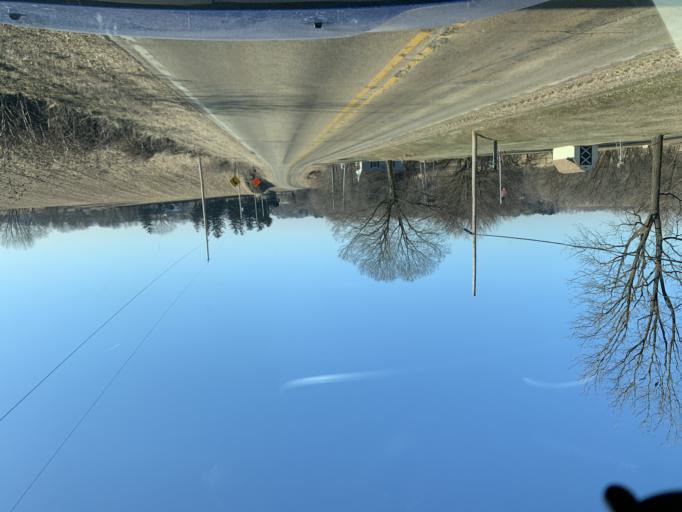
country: US
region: Wisconsin
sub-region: Green County
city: Monroe
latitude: 42.5961
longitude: -89.6013
